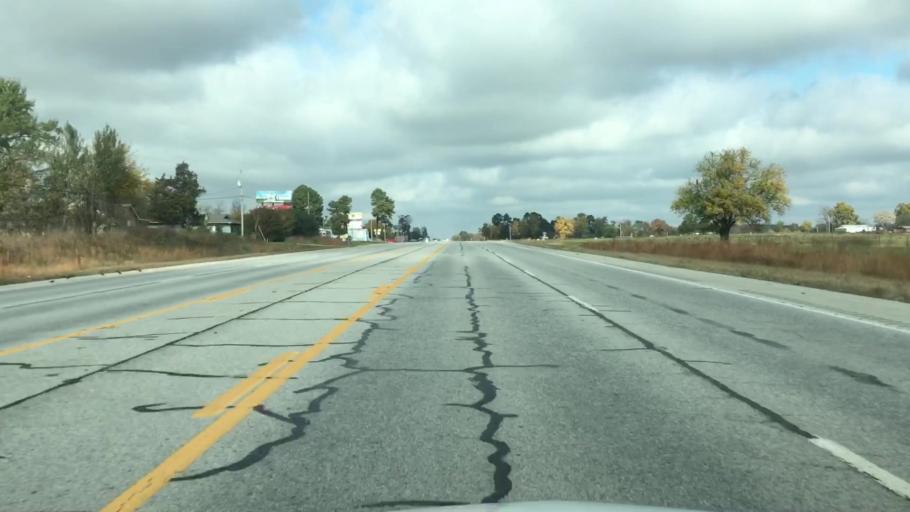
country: US
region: Arkansas
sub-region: Benton County
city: Gentry
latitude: 36.2195
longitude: -94.4954
